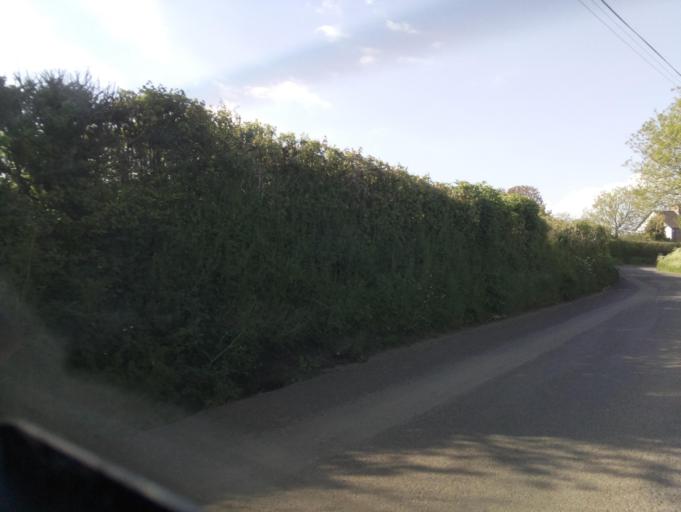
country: GB
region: England
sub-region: Wiltshire
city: Biddestone
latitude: 51.4799
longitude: -2.1741
